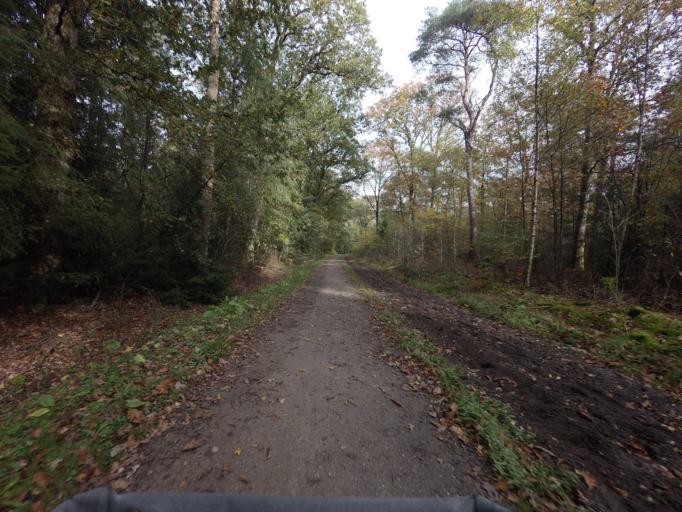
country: NL
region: North Holland
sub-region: Gemeente Hilversum
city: Hilversum
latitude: 52.1937
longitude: 5.2063
